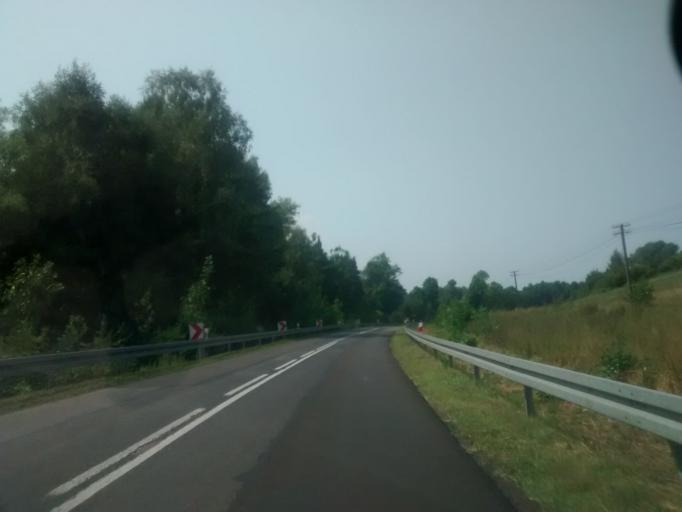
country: PL
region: Silesian Voivodeship
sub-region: Powiat czestochowski
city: Potok Zloty
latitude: 50.7360
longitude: 19.3722
